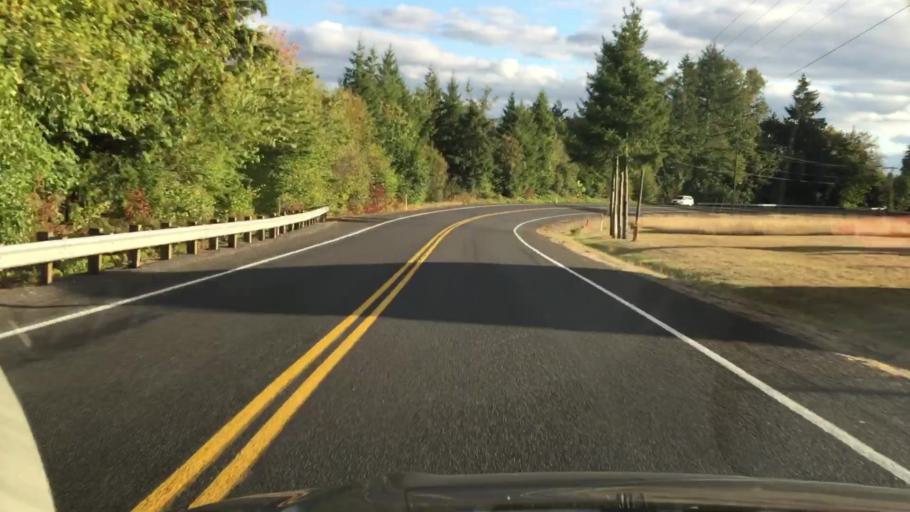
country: US
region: Washington
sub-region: Lewis County
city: Winlock
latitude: 46.4422
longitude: -122.8832
